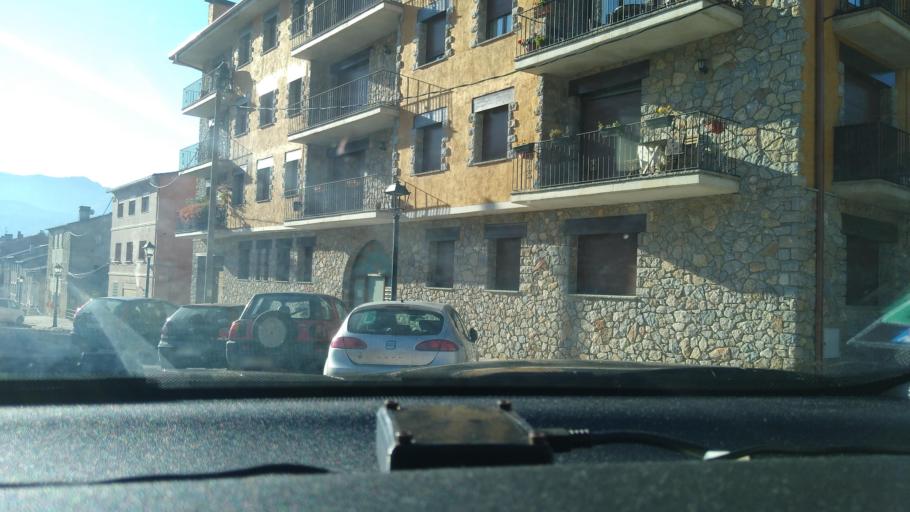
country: ES
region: Catalonia
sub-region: Provincia de Barcelona
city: Baga
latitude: 42.2501
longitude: 1.8652
